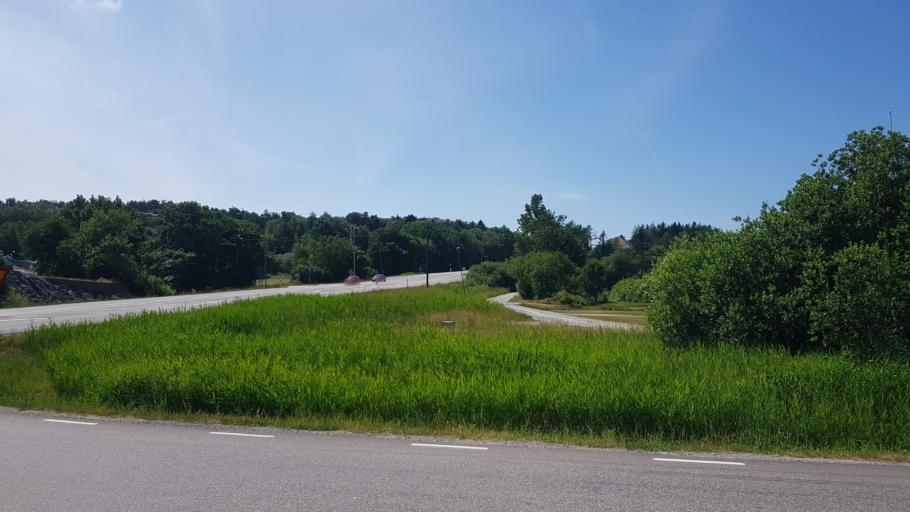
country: SE
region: Vaestra Goetaland
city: Ronnang
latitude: 57.9601
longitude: 11.5846
